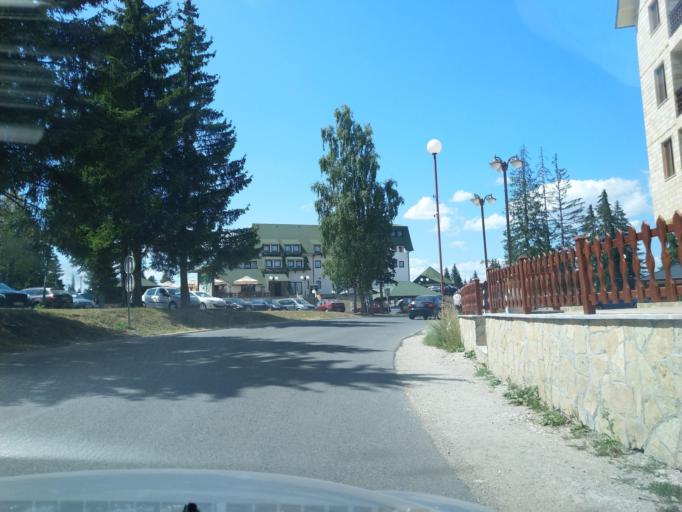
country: RS
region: Central Serbia
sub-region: Zlatiborski Okrug
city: Nova Varos
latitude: 43.4478
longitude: 19.8195
